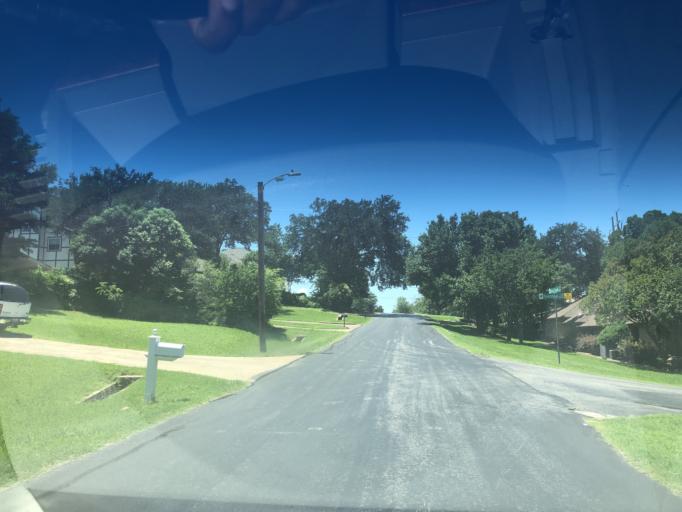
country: US
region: Texas
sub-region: Dallas County
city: Grand Prairie
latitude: 32.7732
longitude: -97.0297
